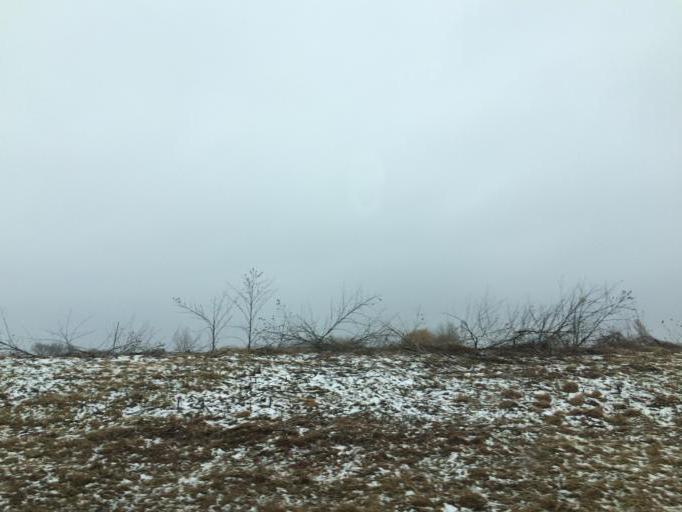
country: US
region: Illinois
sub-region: McHenry County
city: Huntley
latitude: 42.2028
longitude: -88.4225
